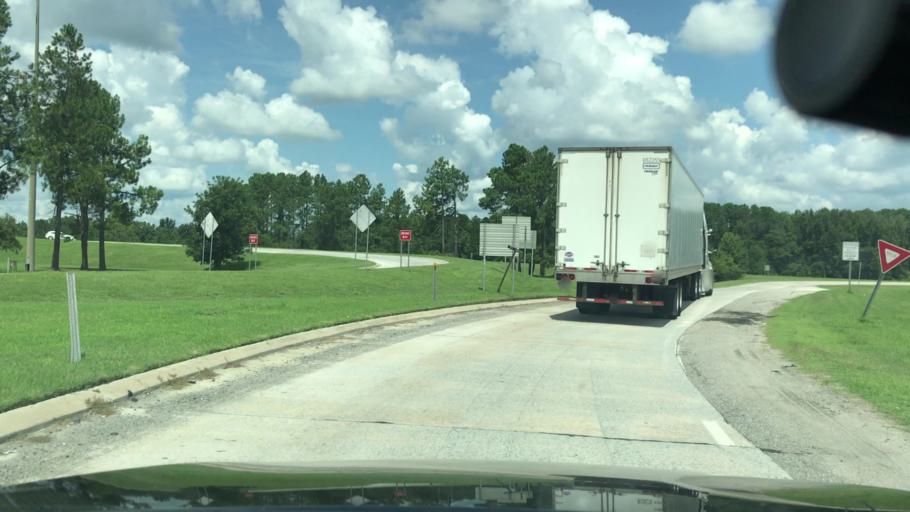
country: US
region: South Carolina
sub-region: Dorchester County
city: Saint George
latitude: 33.1953
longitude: -80.6033
